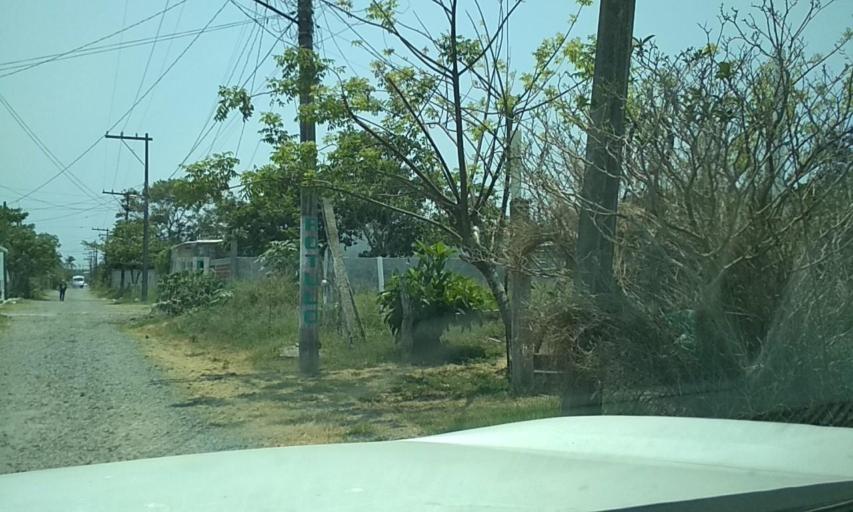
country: MX
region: Veracruz
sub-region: Veracruz
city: Las Amapolas
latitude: 19.1594
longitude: -96.1872
